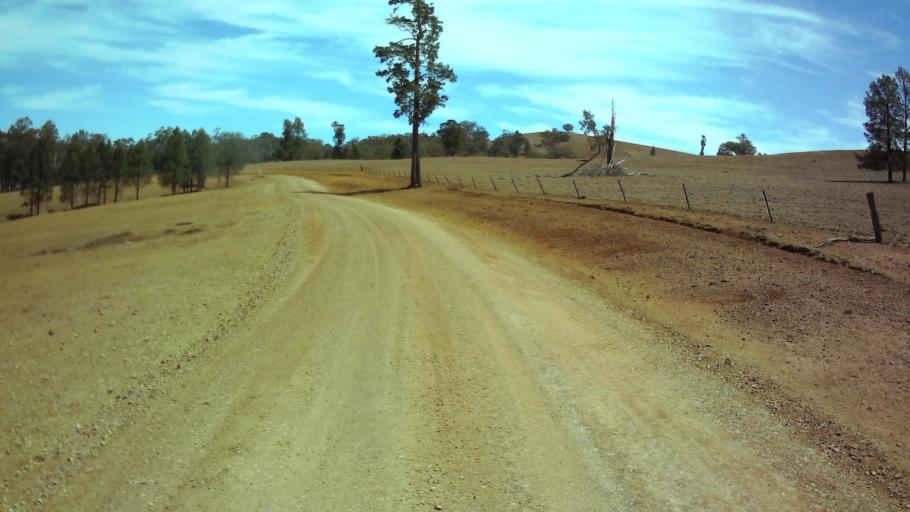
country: AU
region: New South Wales
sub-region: Weddin
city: Grenfell
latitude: -33.7954
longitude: 148.1600
